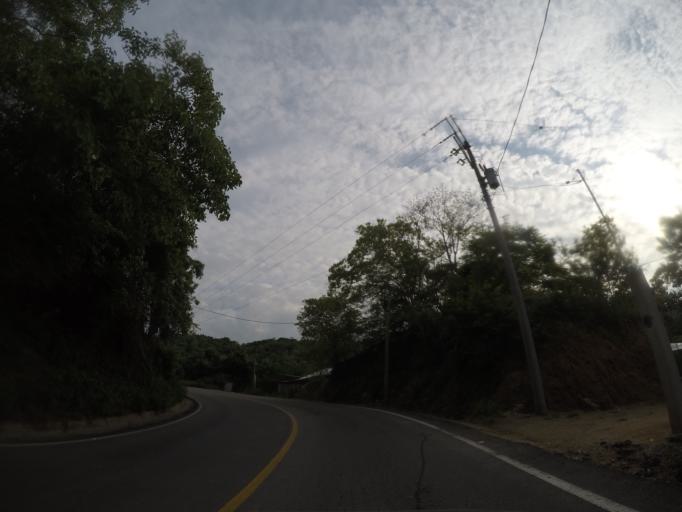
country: MX
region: Oaxaca
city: San Pedro Pochutla
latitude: 15.7024
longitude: -96.4821
